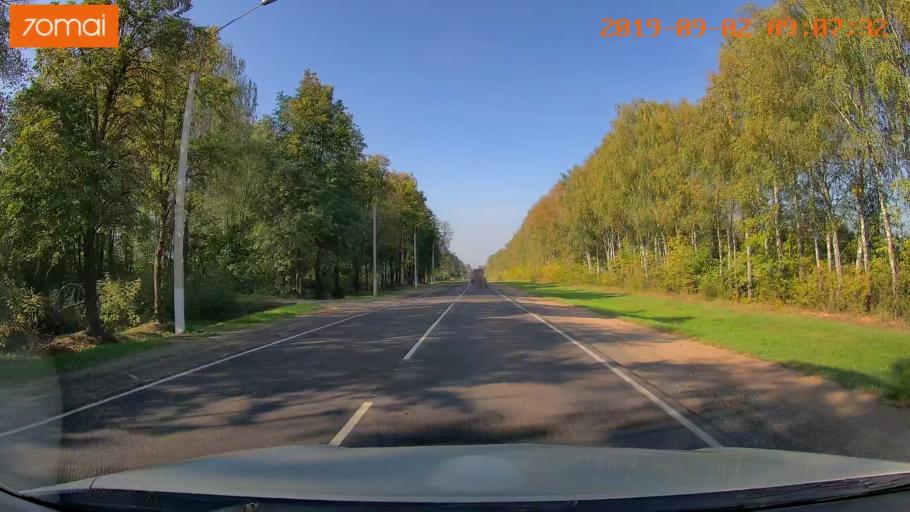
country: RU
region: Kaluga
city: Myatlevo
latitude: 54.8952
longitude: 35.6560
